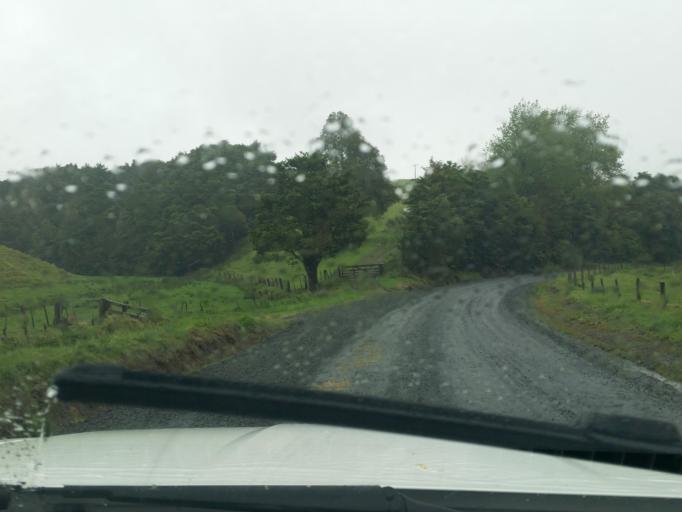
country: NZ
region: Northland
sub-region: Kaipara District
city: Dargaville
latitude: -35.7938
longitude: 173.9760
